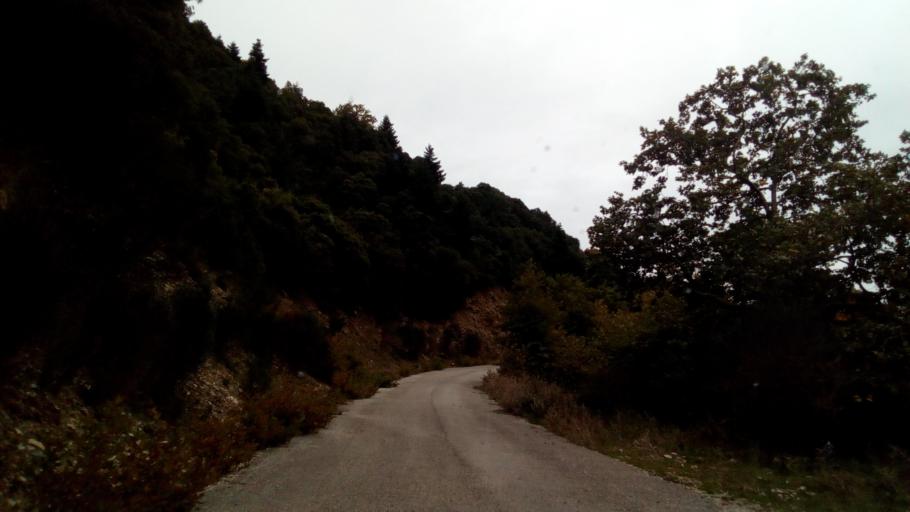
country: GR
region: West Greece
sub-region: Nomos Aitolias kai Akarnanias
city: Thermo
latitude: 38.6194
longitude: 21.8416
